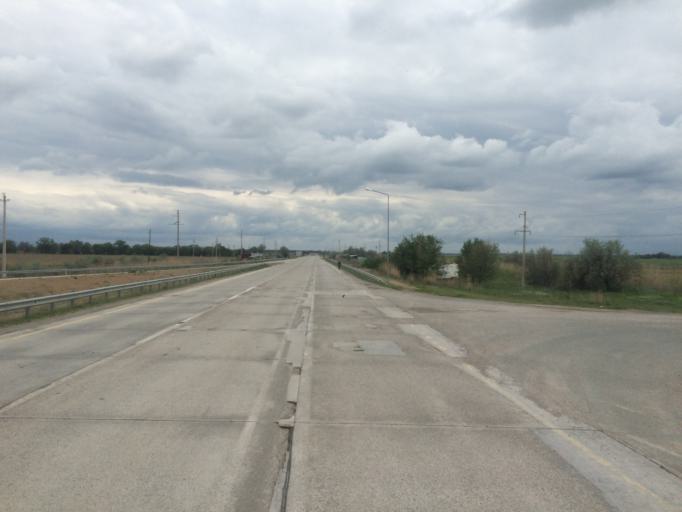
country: KG
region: Chuy
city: Sokuluk
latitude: 43.2730
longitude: 74.2358
